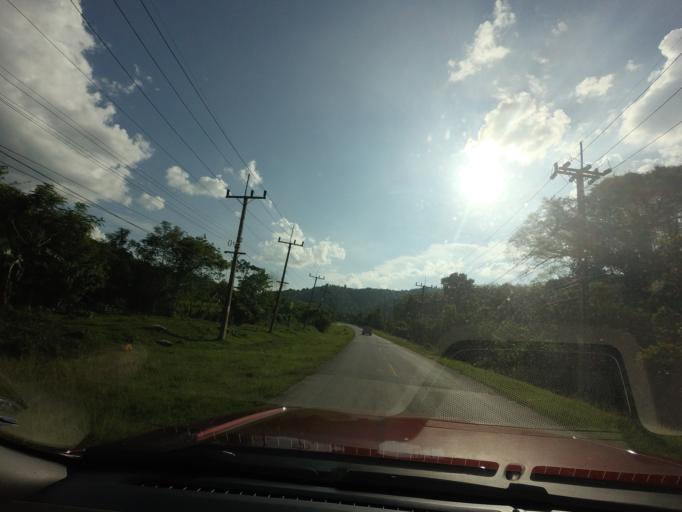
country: TH
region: Yala
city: Ban Nang Sata
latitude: 6.1968
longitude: 101.2580
